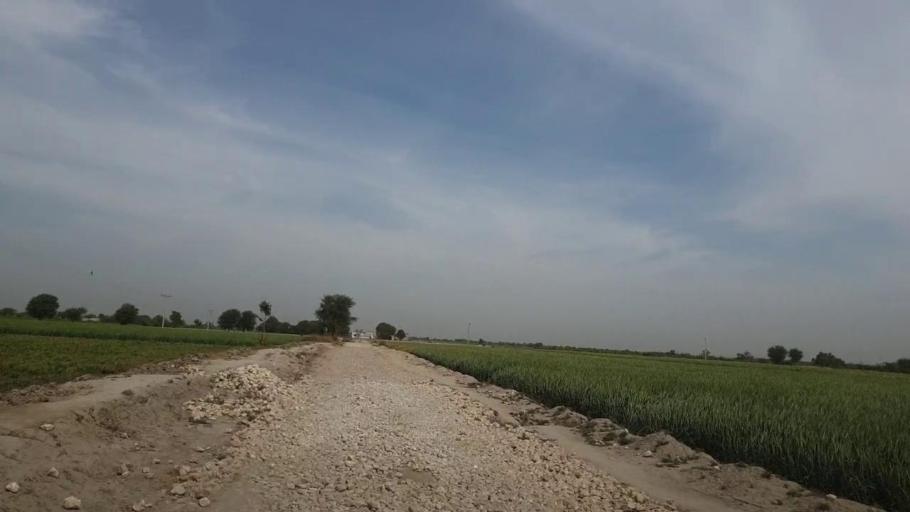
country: PK
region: Sindh
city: Kunri
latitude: 25.1809
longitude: 69.5887
